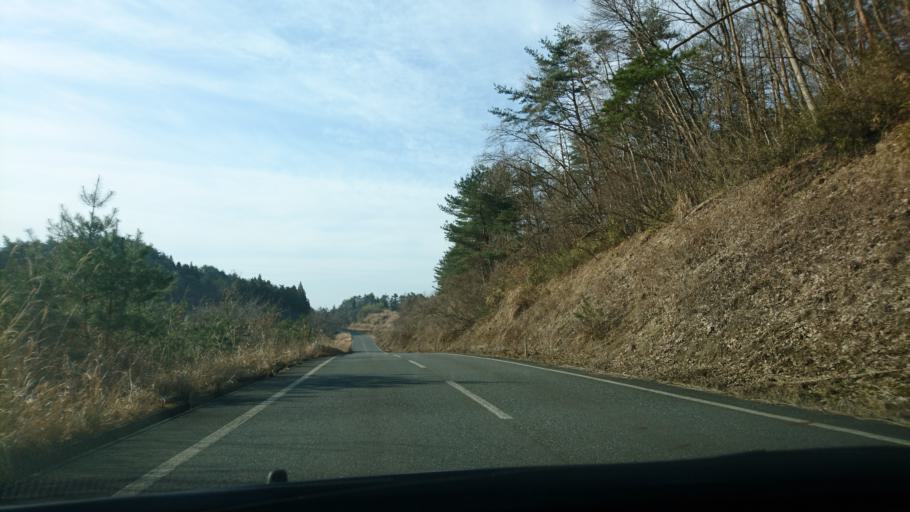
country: JP
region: Iwate
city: Ichinoseki
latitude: 38.8472
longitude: 141.2105
